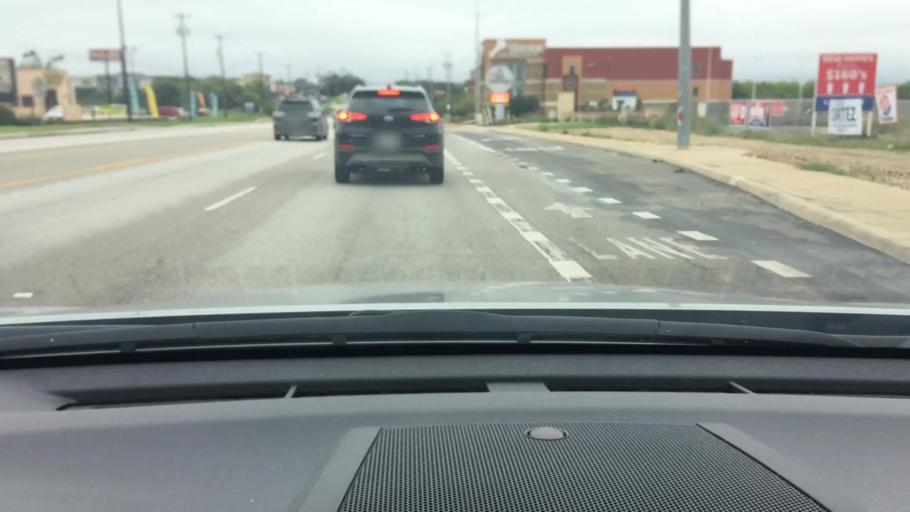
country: US
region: Texas
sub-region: Bexar County
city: Helotes
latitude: 29.5011
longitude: -98.7226
